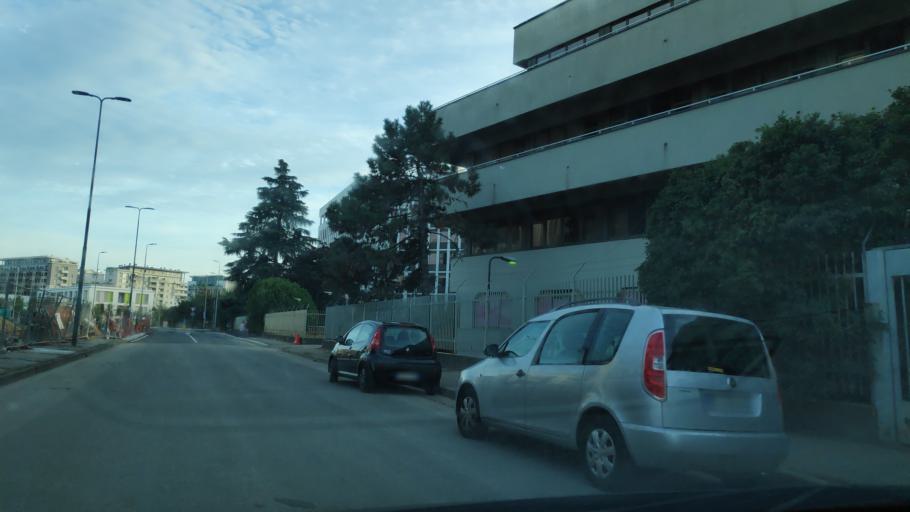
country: IT
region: Lombardy
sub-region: Citta metropolitana di Milano
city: Chiaravalle
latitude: 45.4413
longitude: 9.2394
